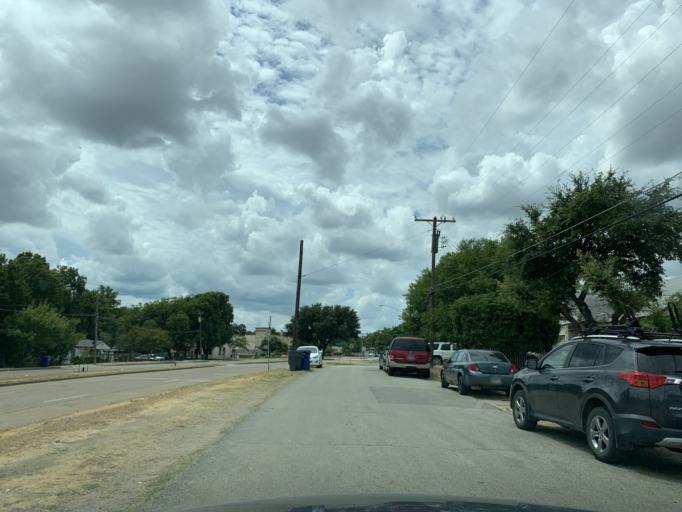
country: US
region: Texas
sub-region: Dallas County
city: Cockrell Hill
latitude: 32.7411
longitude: -96.8774
